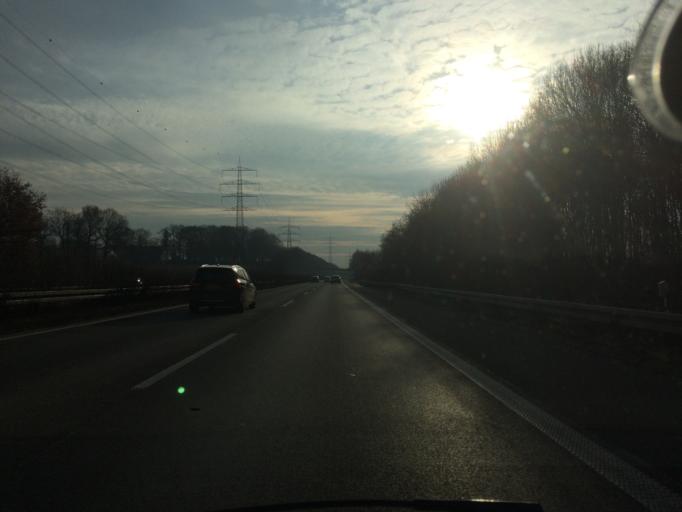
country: DE
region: North Rhine-Westphalia
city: Dorsten
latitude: 51.6159
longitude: 6.9381
